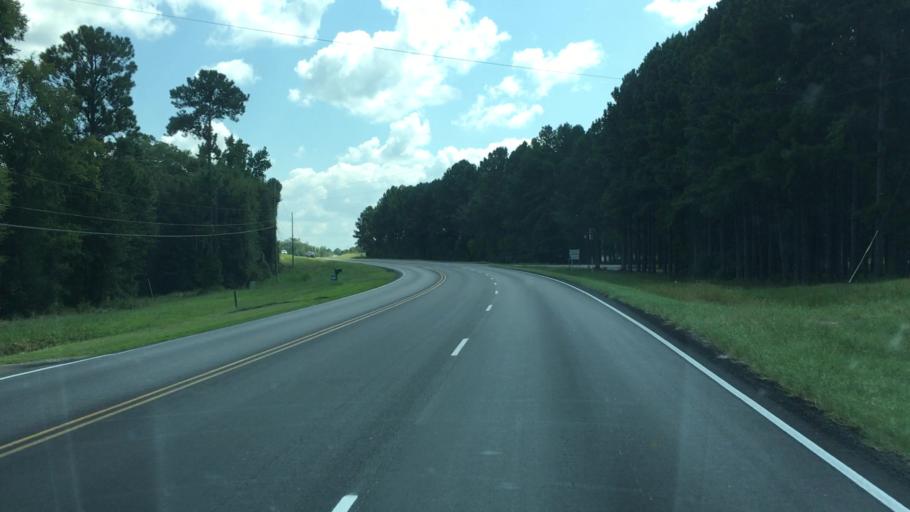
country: US
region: Georgia
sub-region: Morgan County
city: Madison
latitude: 33.6320
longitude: -83.4508
